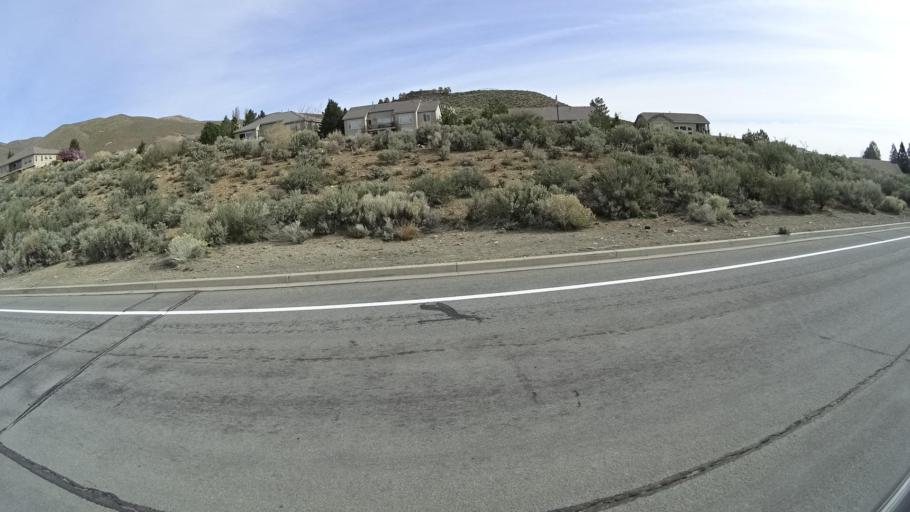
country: US
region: Nevada
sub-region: Washoe County
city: Mogul
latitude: 39.5470
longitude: -119.8947
